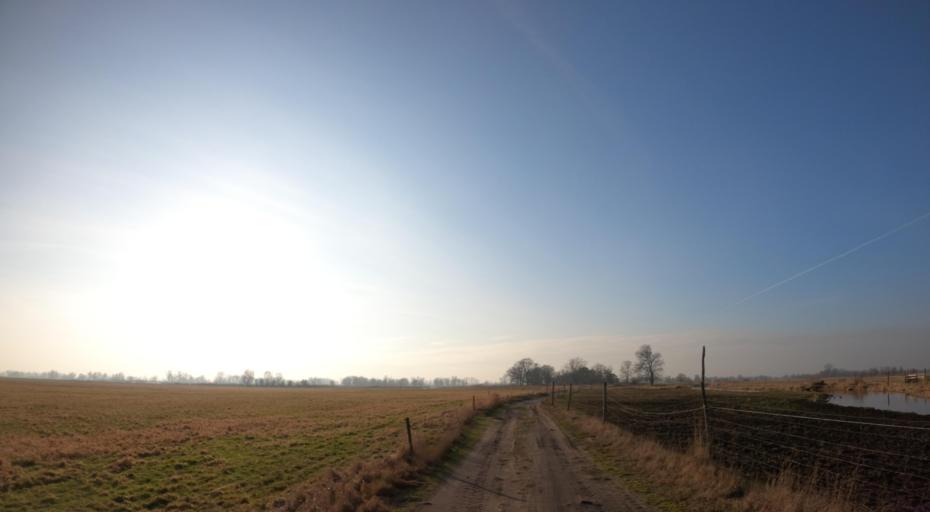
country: DE
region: Brandenburg
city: Zechin
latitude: 52.6592
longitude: 14.4971
